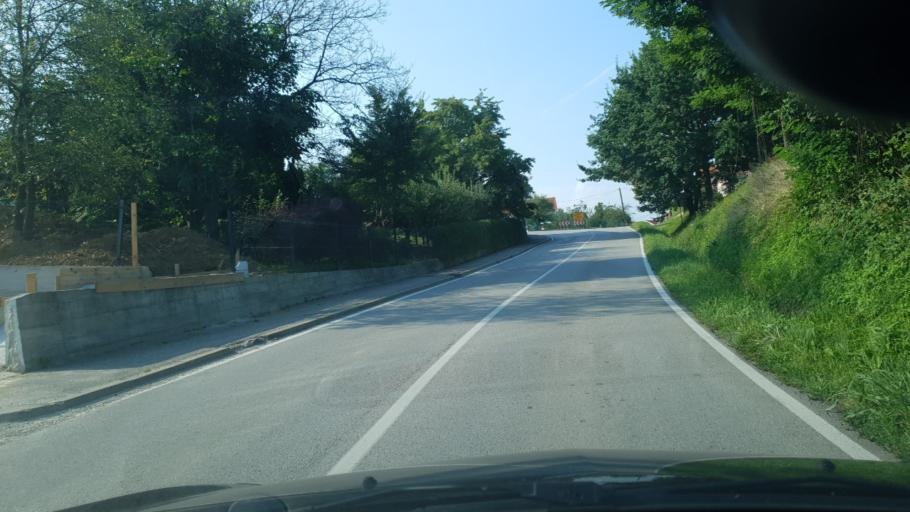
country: HR
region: Krapinsko-Zagorska
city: Oroslavje
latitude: 45.9776
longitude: 15.9211
